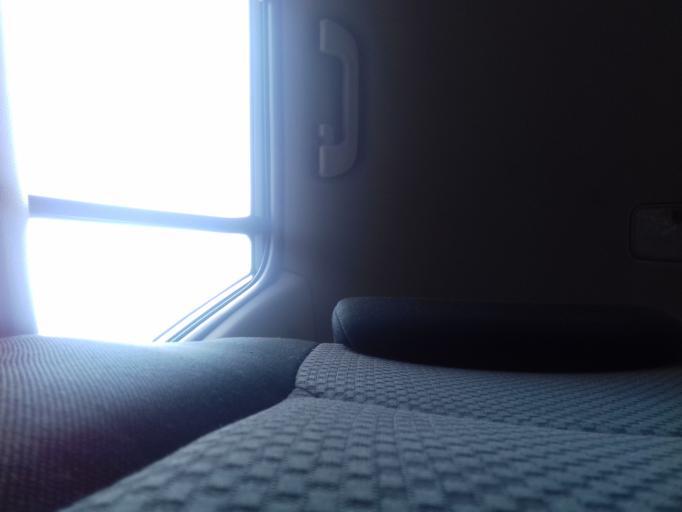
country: IE
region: Leinster
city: Portraine
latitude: 53.4790
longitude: -6.1169
